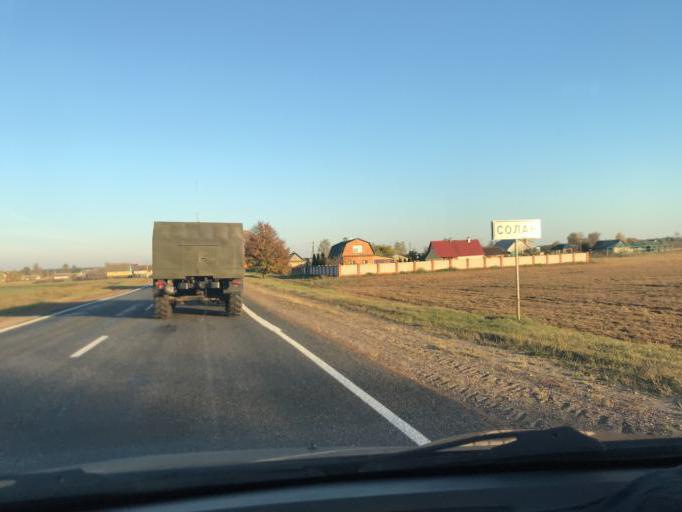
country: BY
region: Minsk
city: Staryya Darohi
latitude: 53.0468
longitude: 28.1005
